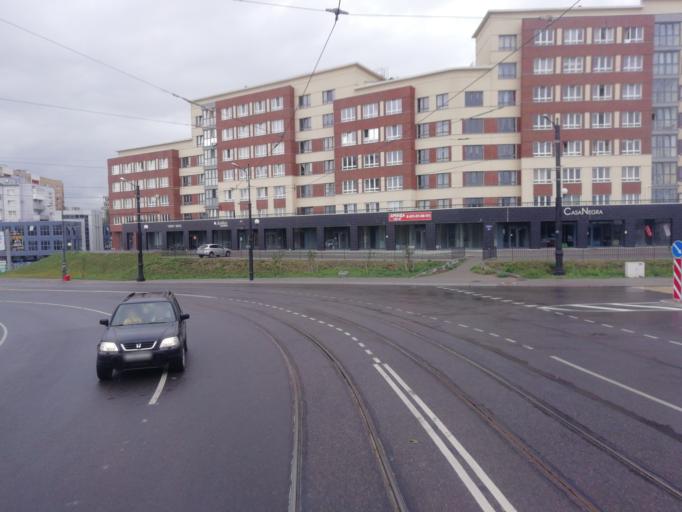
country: RU
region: Kaliningrad
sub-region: Gorod Kaliningrad
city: Kaliningrad
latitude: 54.6997
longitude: 20.5180
